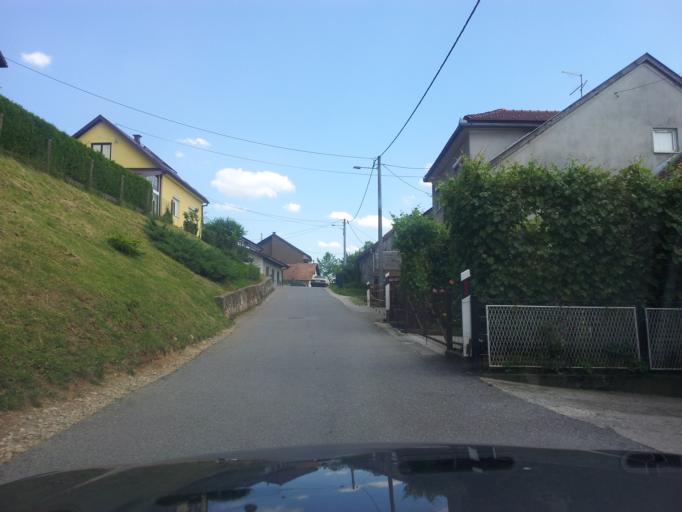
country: HR
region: Karlovacka
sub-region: Grad Karlovac
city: Karlovac
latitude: 45.4553
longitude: 15.4985
